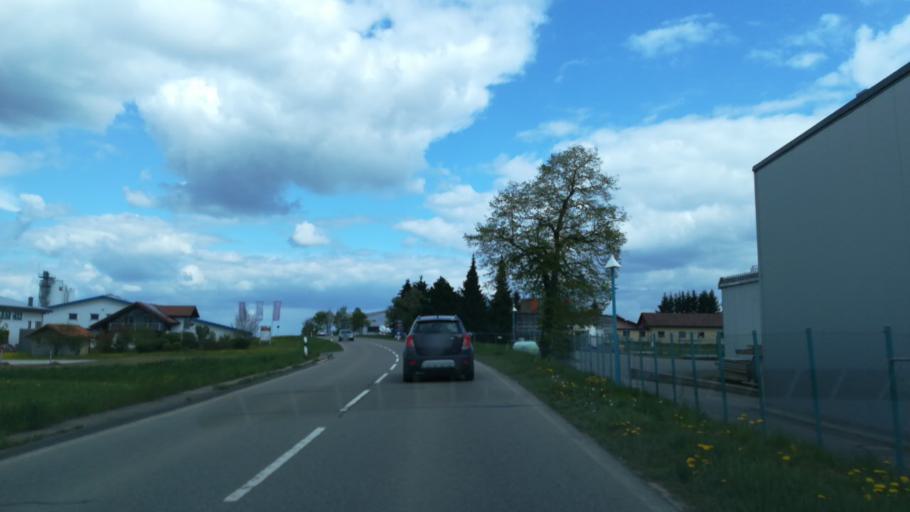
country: DE
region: Baden-Wuerttemberg
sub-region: Freiburg Region
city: Bonndorf im Schwarzwald
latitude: 47.8210
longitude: 8.3508
